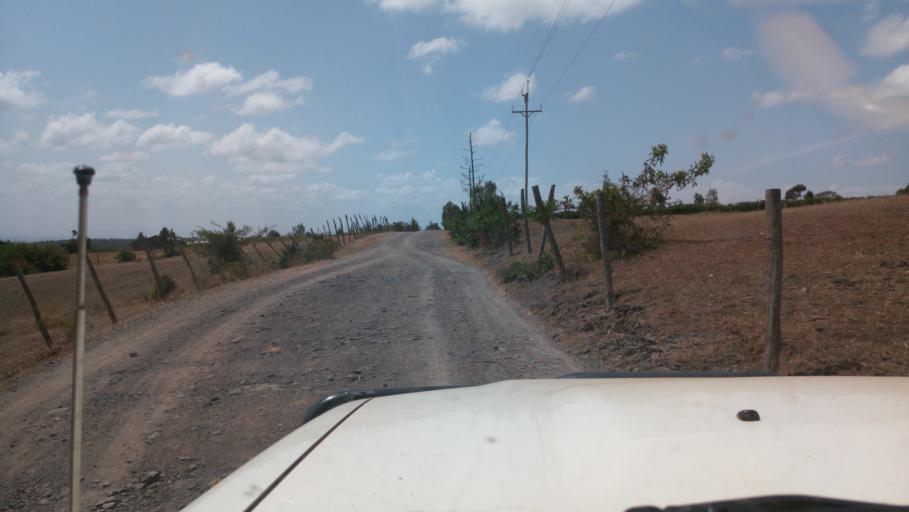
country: KE
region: Laikipia
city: Naro Moru
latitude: -0.1764
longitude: 36.7963
